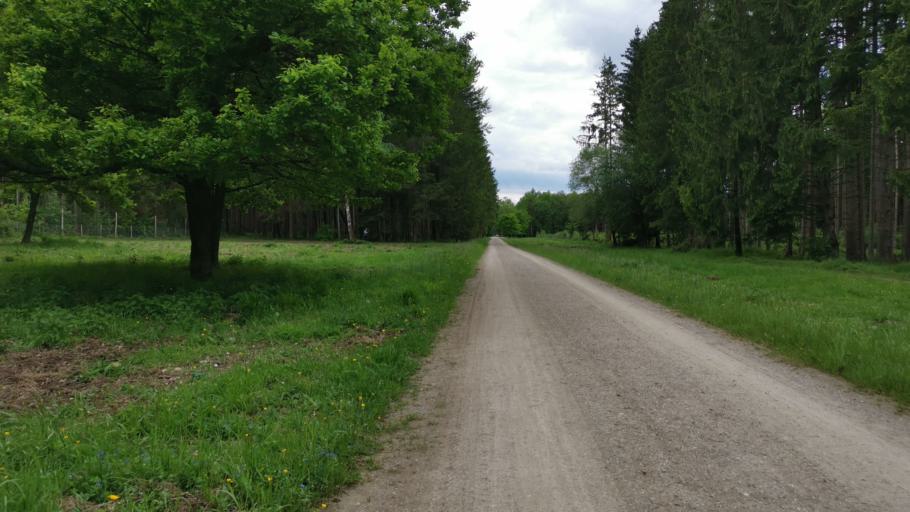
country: DE
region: Bavaria
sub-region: Upper Bavaria
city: Pullach im Isartal
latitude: 48.0637
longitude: 11.5015
